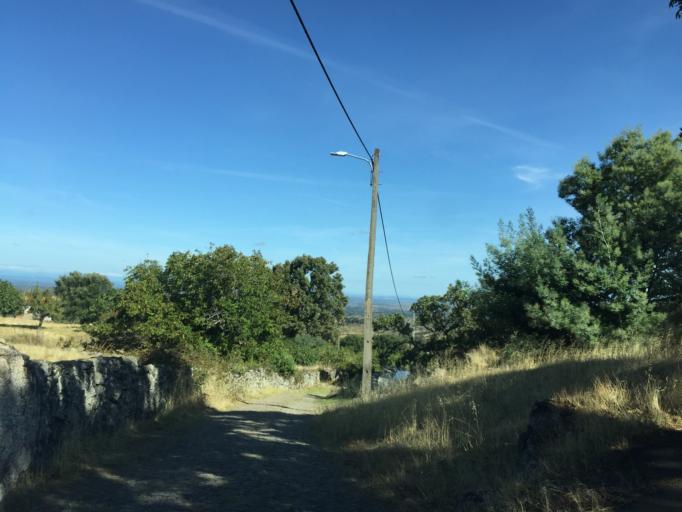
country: PT
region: Portalegre
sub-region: Marvao
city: Marvao
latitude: 39.3987
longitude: -7.3683
